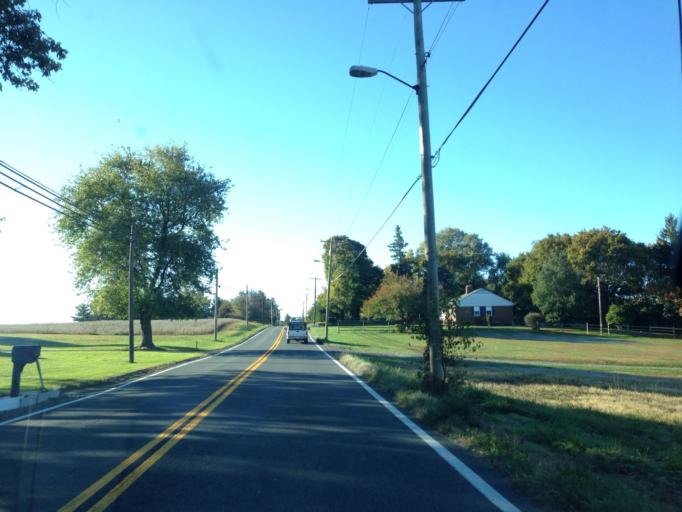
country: US
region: Maryland
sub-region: Montgomery County
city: Damascus
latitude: 39.3159
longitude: -77.1982
